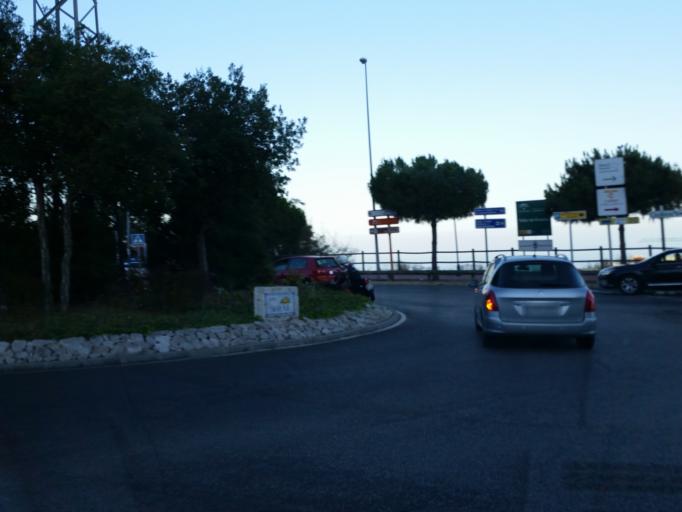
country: ES
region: Andalusia
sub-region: Provincia de Malaga
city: Benalmadena
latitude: 36.6074
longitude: -4.5407
